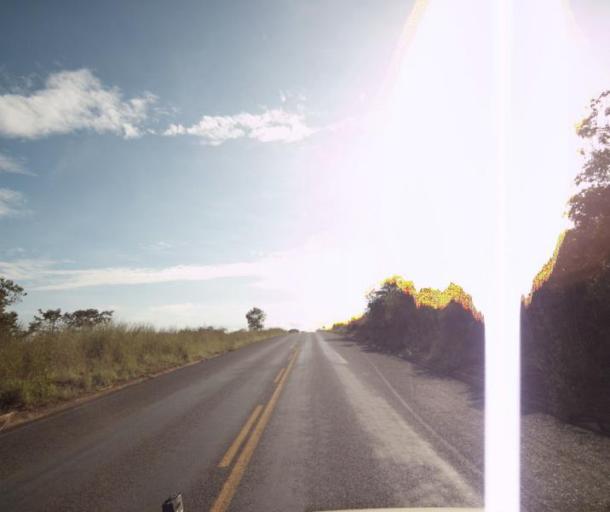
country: BR
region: Goias
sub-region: Pirenopolis
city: Pirenopolis
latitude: -15.5798
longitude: -48.6277
